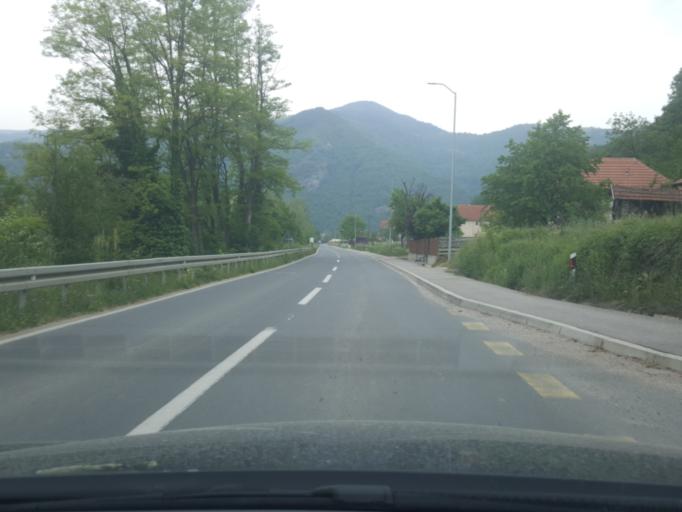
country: RS
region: Central Serbia
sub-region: Zlatiborski Okrug
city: Bajina Basta
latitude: 43.9903
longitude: 19.5685
